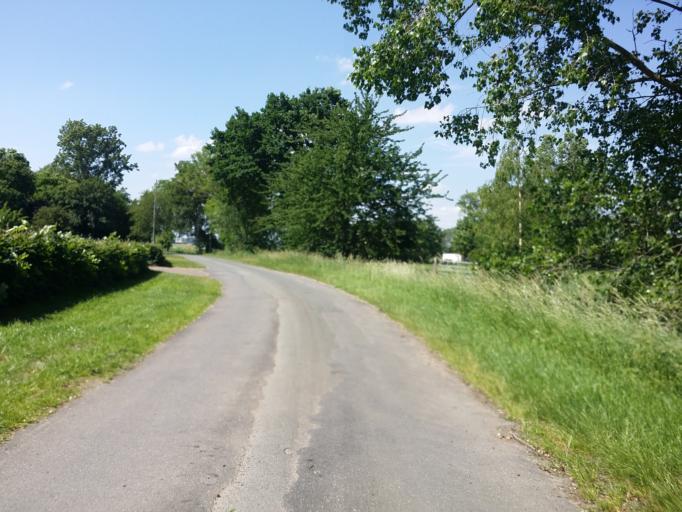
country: DE
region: Lower Saxony
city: Lemwerder
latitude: 53.1514
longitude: 8.5476
